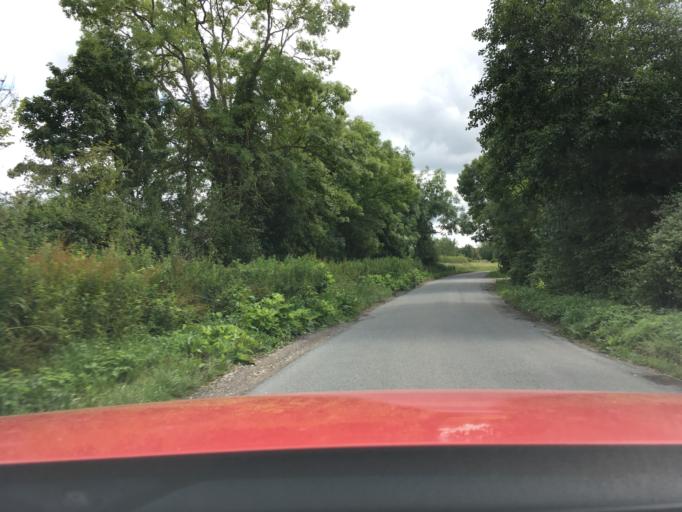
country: GB
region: England
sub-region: Gloucestershire
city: Stonehouse
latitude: 51.8162
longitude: -2.3442
